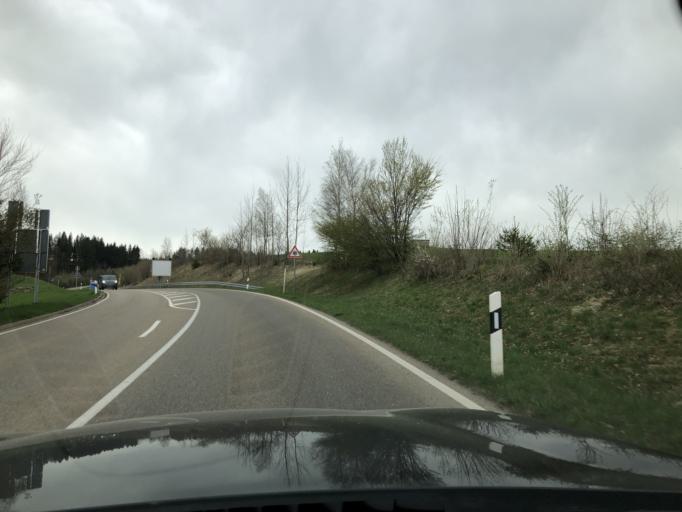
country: DE
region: Bavaria
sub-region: Swabia
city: Nesselwang
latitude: 47.6387
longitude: 10.5281
